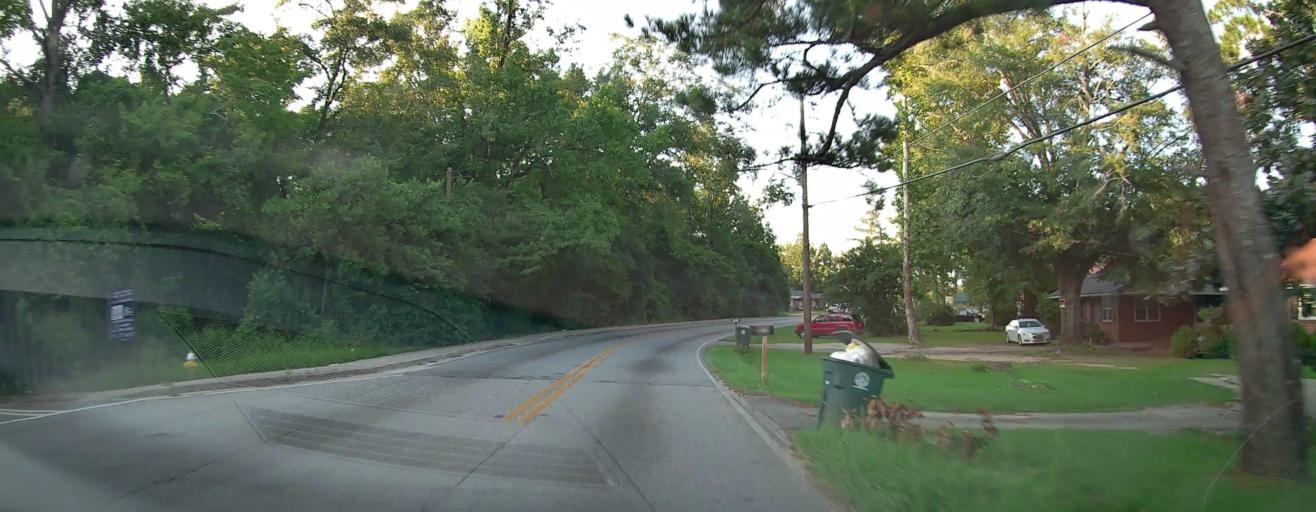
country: US
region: Georgia
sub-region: Bibb County
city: Macon
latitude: 32.8273
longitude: -83.7096
